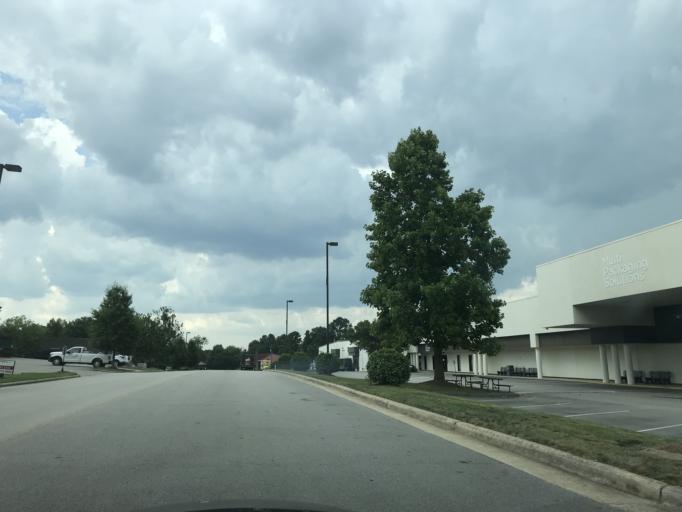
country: US
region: North Carolina
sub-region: Wake County
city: Wake Forest
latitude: 35.8868
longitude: -78.5827
